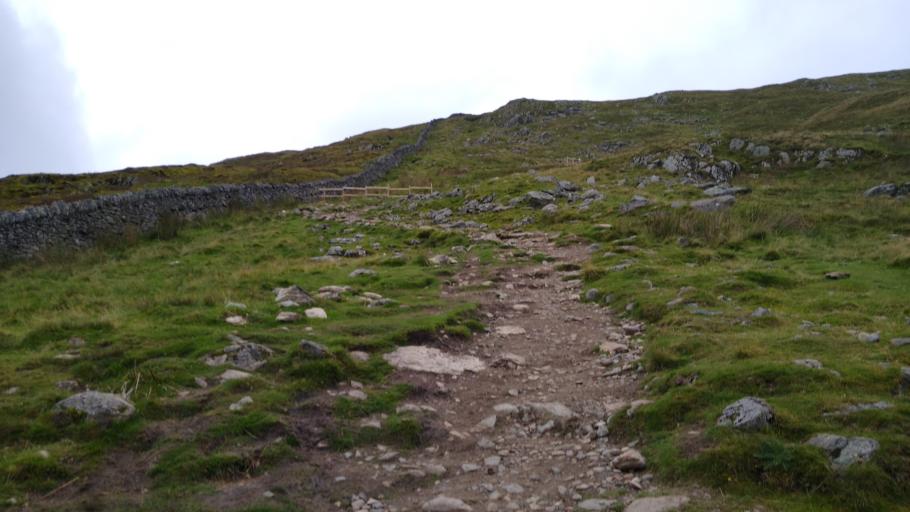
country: GB
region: England
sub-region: Cumbria
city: Ambleside
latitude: 54.5357
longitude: -2.9777
